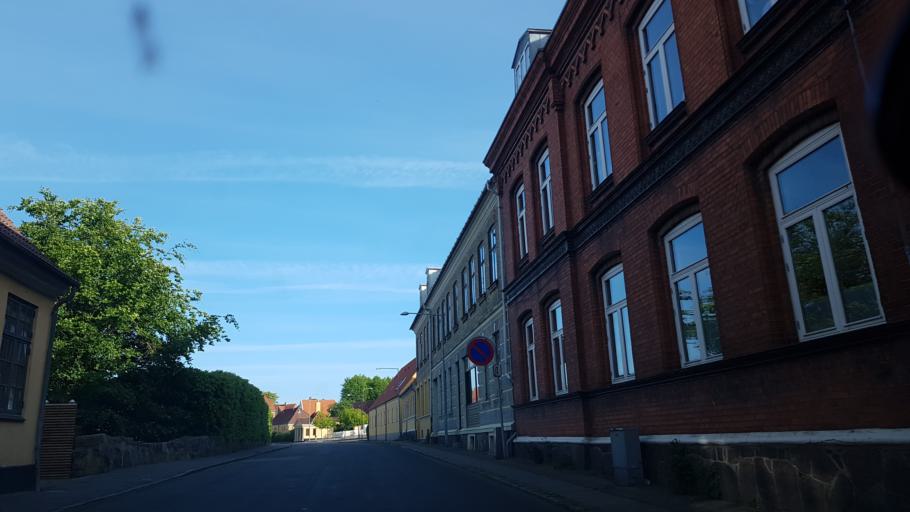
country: DK
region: Zealand
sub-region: Slagelse Kommune
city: Korsor
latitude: 55.3273
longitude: 11.1405
